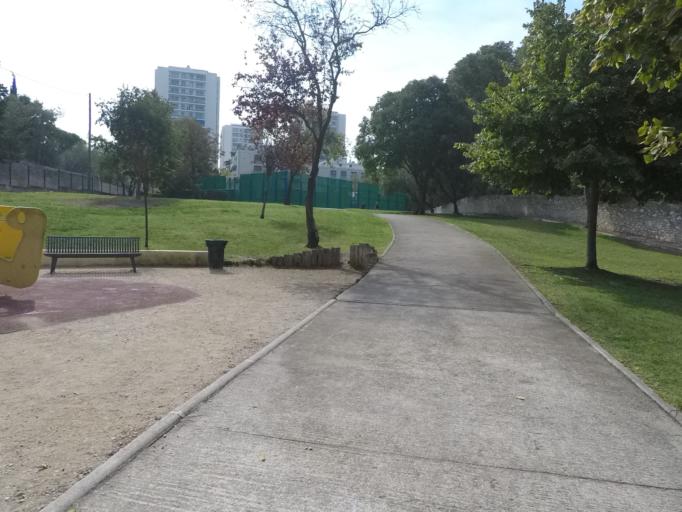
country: FR
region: Provence-Alpes-Cote d'Azur
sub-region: Departement des Bouches-du-Rhone
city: Marseille 09
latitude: 43.2566
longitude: 5.4166
